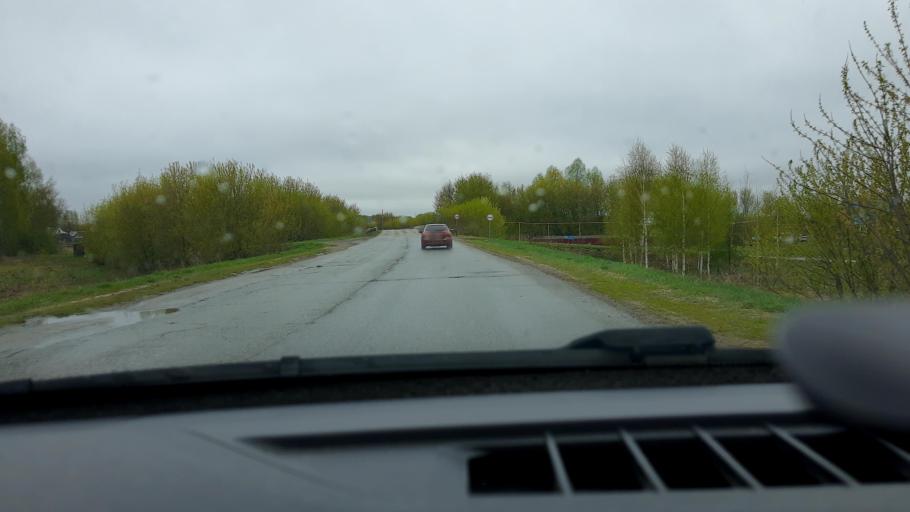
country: RU
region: Nizjnij Novgorod
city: Perevoz
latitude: 55.5926
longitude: 44.6486
